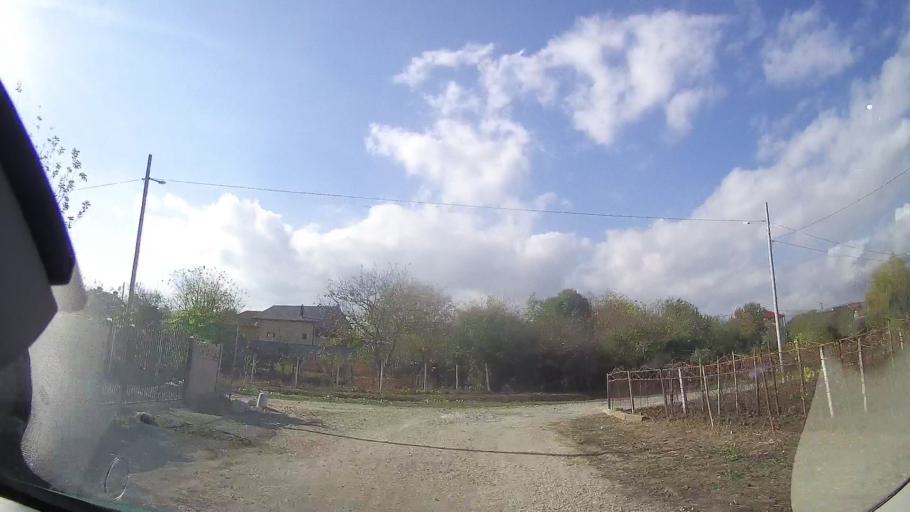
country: RO
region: Constanta
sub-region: Comuna Douazeci si Trei August
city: Douazeci si Trei August
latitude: 43.9142
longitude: 28.5817
